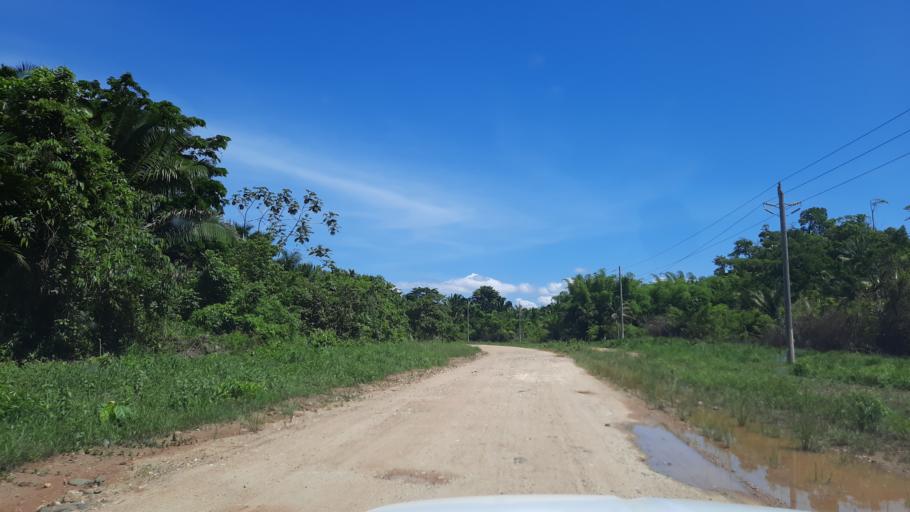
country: BZ
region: Stann Creek
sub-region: Dangriga
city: Dangriga
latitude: 17.1785
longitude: -88.3985
